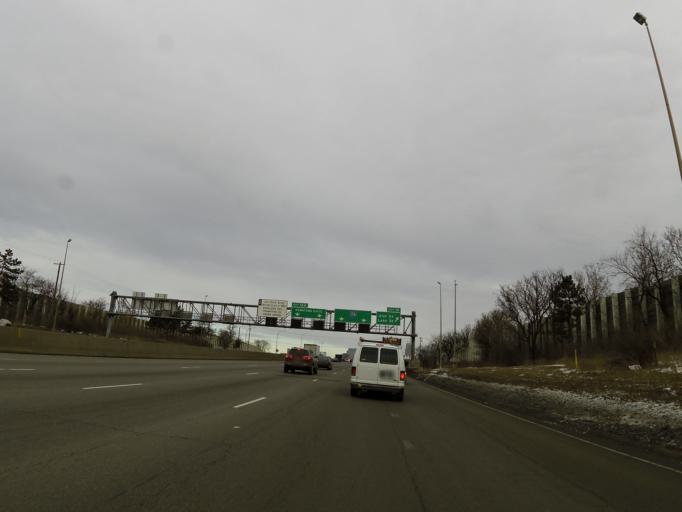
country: US
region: Minnesota
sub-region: Hennepin County
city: Minneapolis
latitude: 44.9428
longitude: -93.2745
